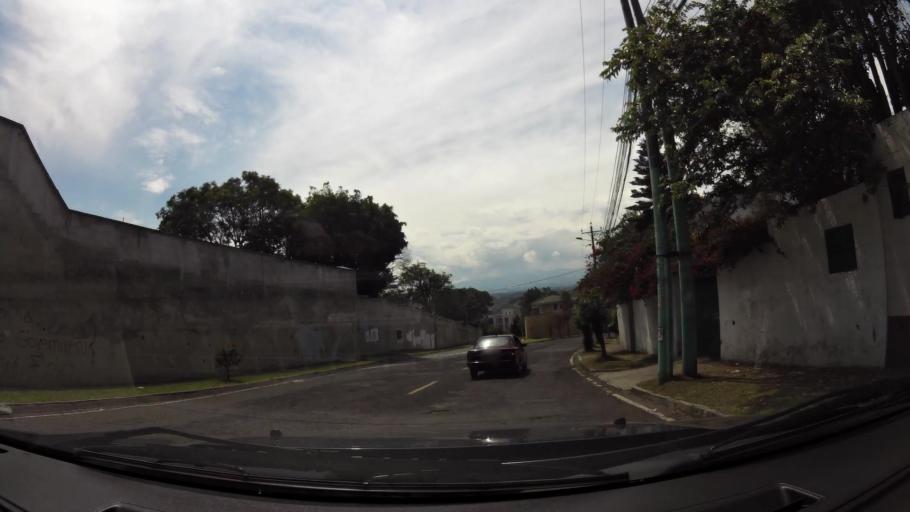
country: EC
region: Pichincha
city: Quito
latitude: -0.2118
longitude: -78.4299
